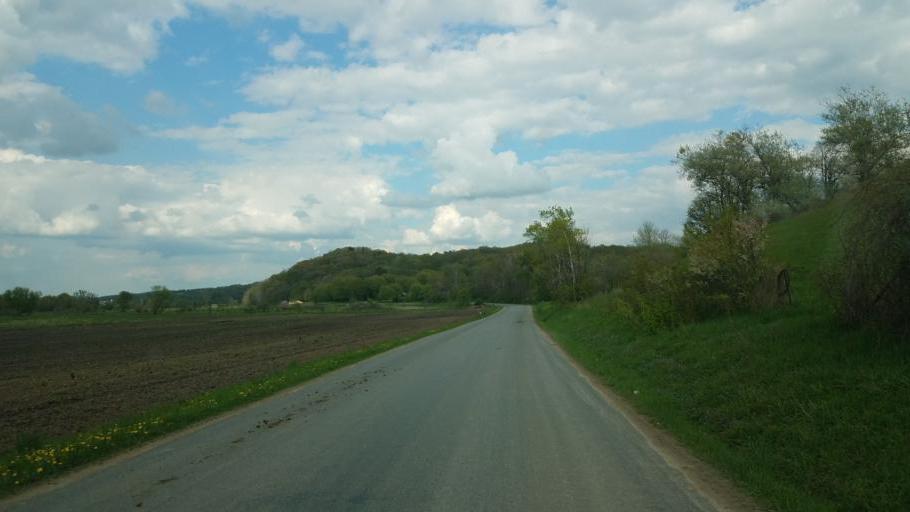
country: US
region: Wisconsin
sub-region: Vernon County
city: Hillsboro
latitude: 43.6194
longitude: -90.3759
